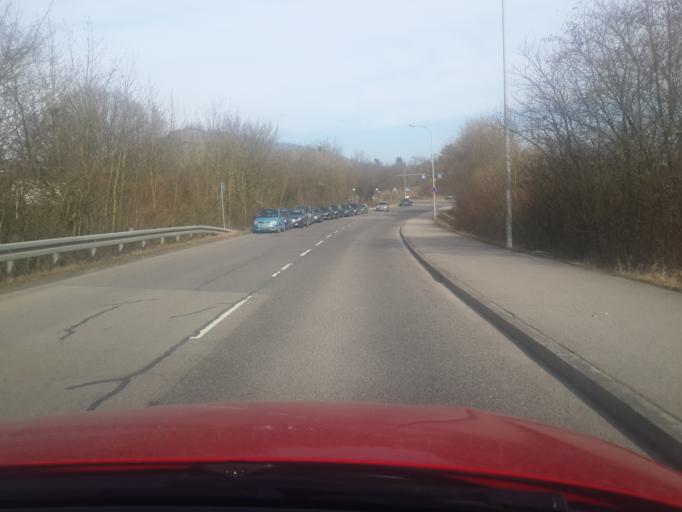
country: DE
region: Baden-Wuerttemberg
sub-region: Regierungsbezirk Stuttgart
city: Neckarsulm
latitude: 49.1883
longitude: 9.2437
